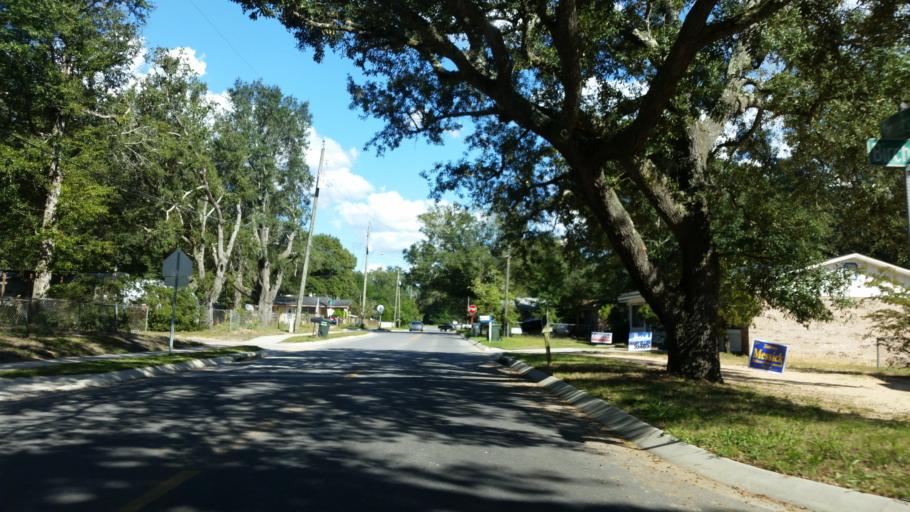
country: US
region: Florida
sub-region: Santa Rosa County
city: Milton
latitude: 30.6384
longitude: -87.0460
